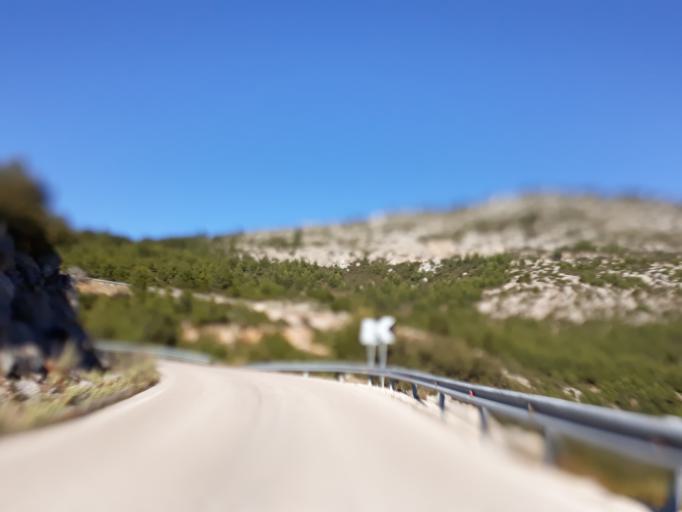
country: GR
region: Attica
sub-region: Nomarchia Dytikis Attikis
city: Fyli
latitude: 38.1312
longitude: 23.6491
